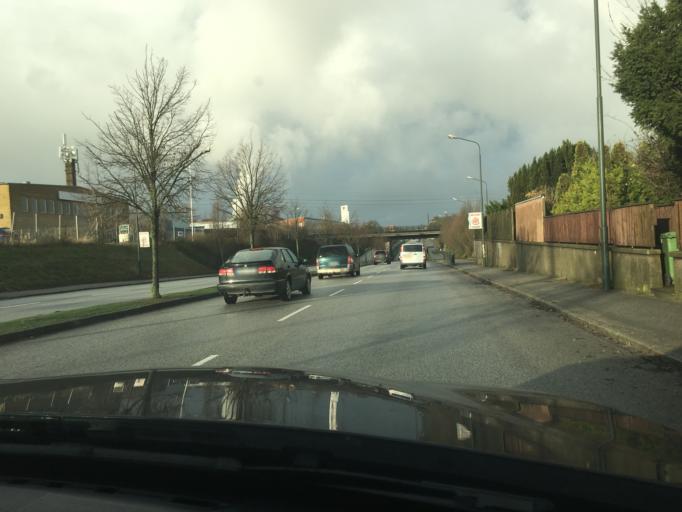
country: SE
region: Skane
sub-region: Malmo
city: Malmoe
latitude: 55.5746
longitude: 13.0318
